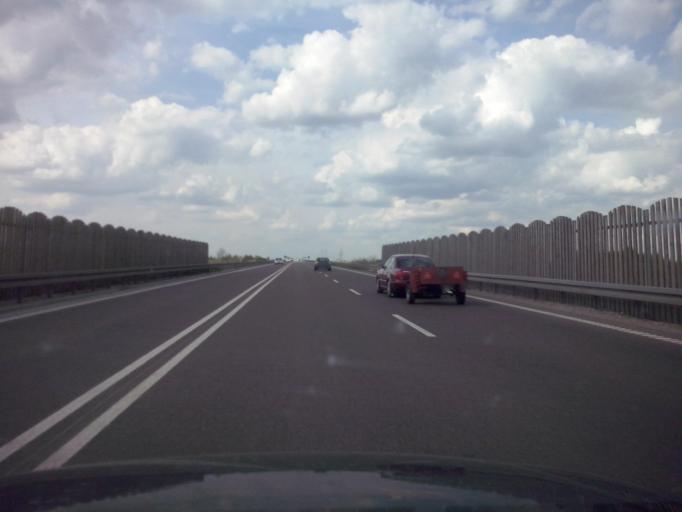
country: PL
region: Subcarpathian Voivodeship
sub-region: Powiat rzeszowski
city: Wolka Podlesna
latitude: 50.1320
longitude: 22.0803
